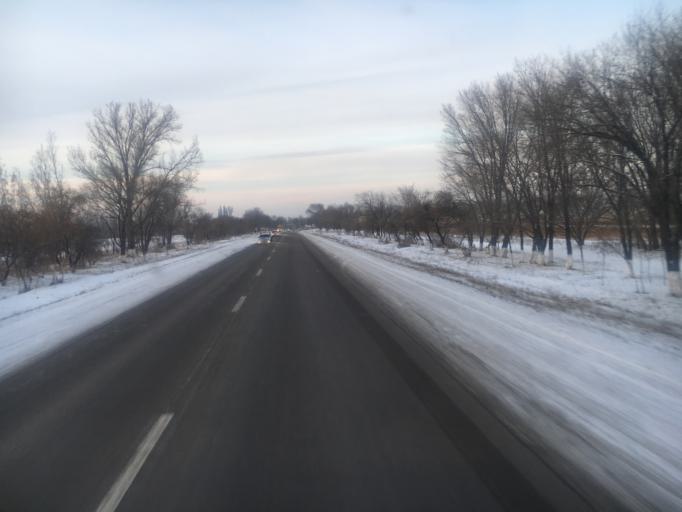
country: KZ
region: Almaty Oblysy
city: Burunday
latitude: 43.3619
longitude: 76.6432
